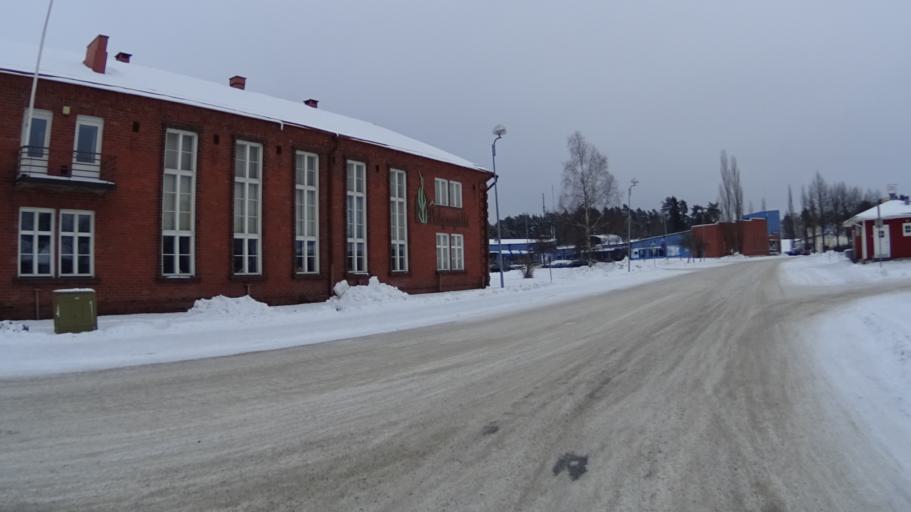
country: FI
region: Uusimaa
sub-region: Helsinki
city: Karkkila
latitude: 60.5360
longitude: 24.2118
